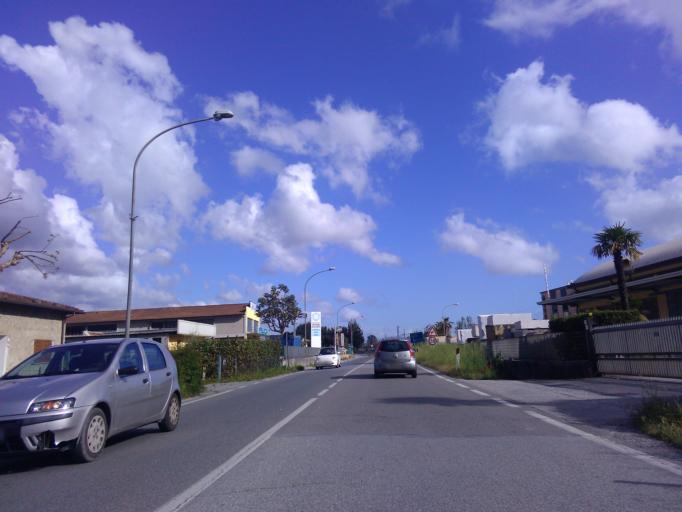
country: IT
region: Tuscany
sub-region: Provincia di Lucca
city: Strettoia
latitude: 43.9928
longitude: 10.1797
